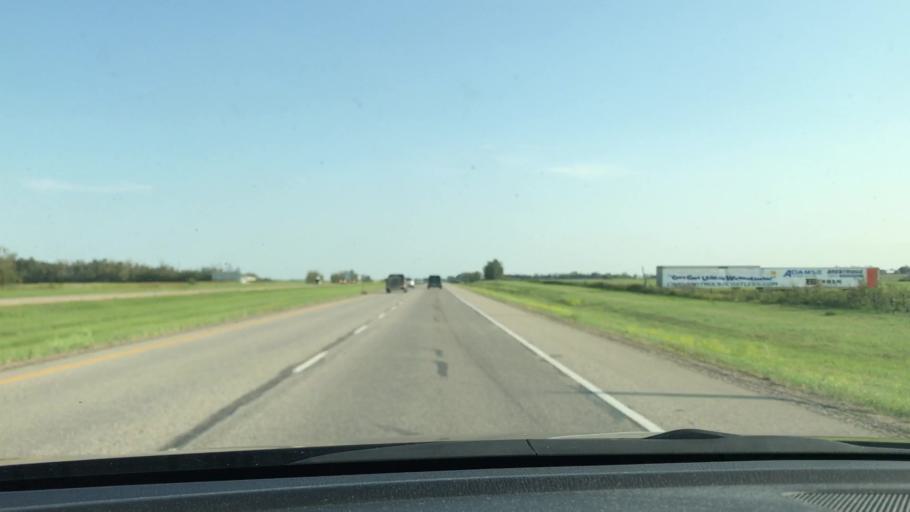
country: CA
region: Alberta
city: Millet
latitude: 53.0842
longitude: -113.5984
